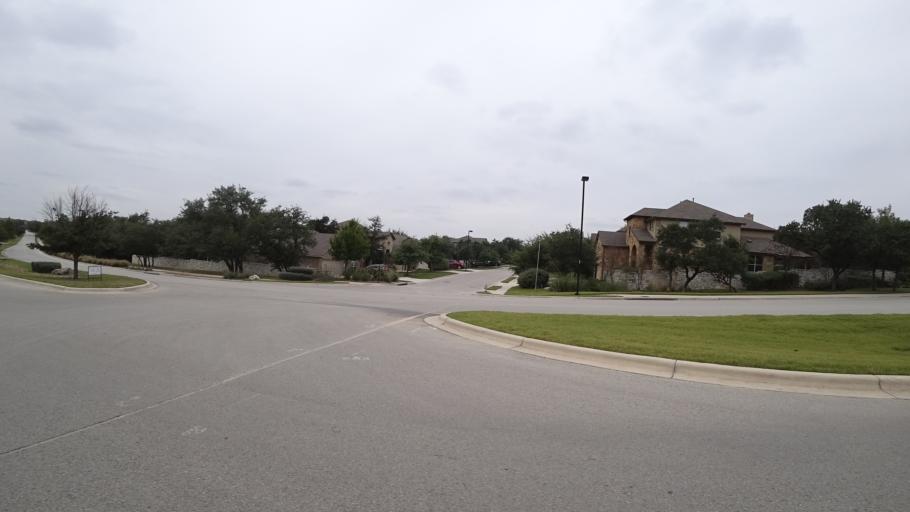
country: US
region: Texas
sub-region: Travis County
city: Shady Hollow
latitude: 30.1801
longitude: -97.9007
